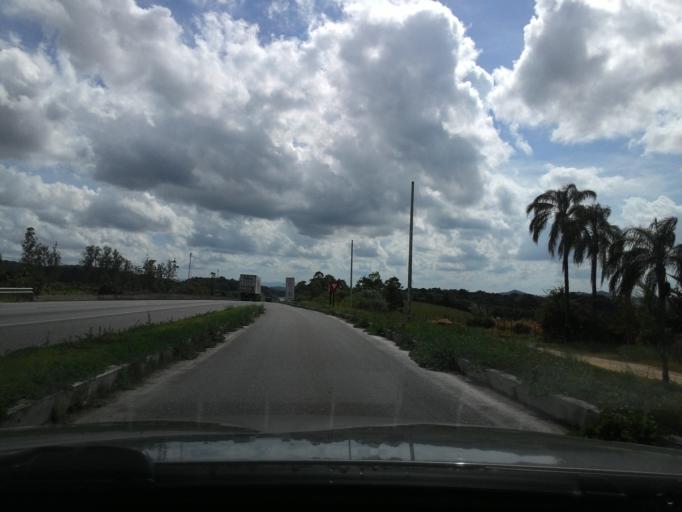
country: BR
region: Sao Paulo
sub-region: Jacupiranga
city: Jacupiranga
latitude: -24.6518
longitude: -47.9481
